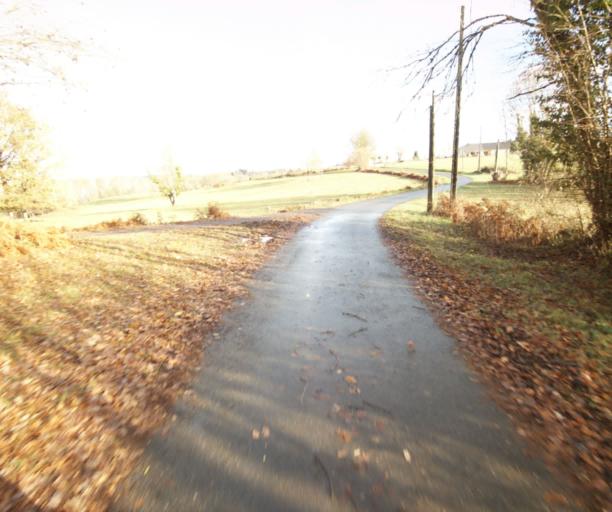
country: FR
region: Limousin
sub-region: Departement de la Correze
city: Saint-Mexant
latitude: 45.2564
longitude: 1.6183
